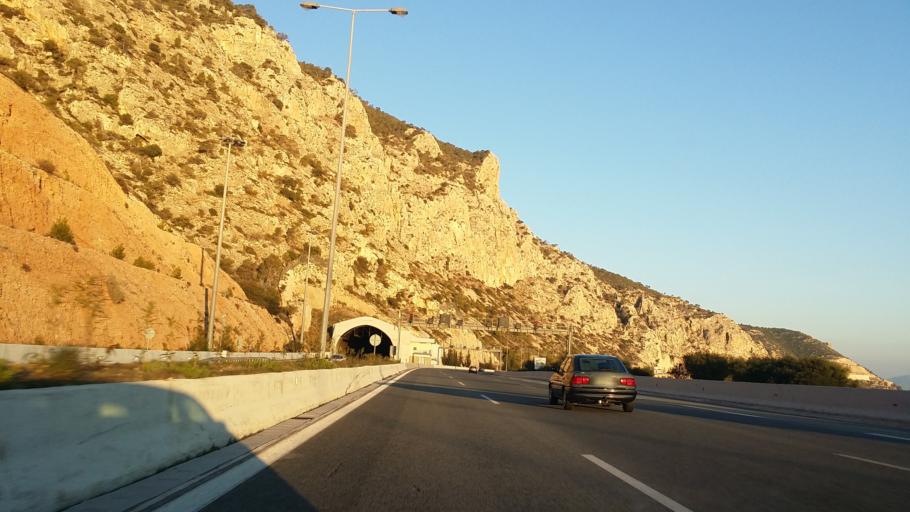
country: GR
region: Attica
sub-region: Nomarchia Dytikis Attikis
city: Kineta
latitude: 37.9787
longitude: 23.2639
